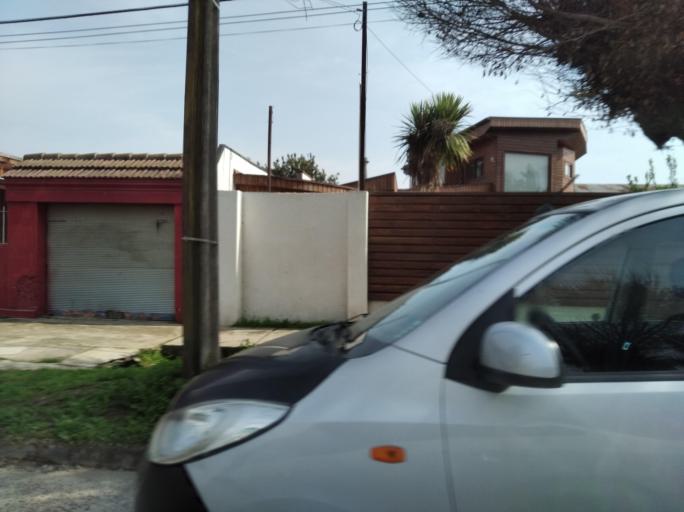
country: CL
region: Valparaiso
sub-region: Provincia de Marga Marga
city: Limache
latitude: -32.9875
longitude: -71.2790
